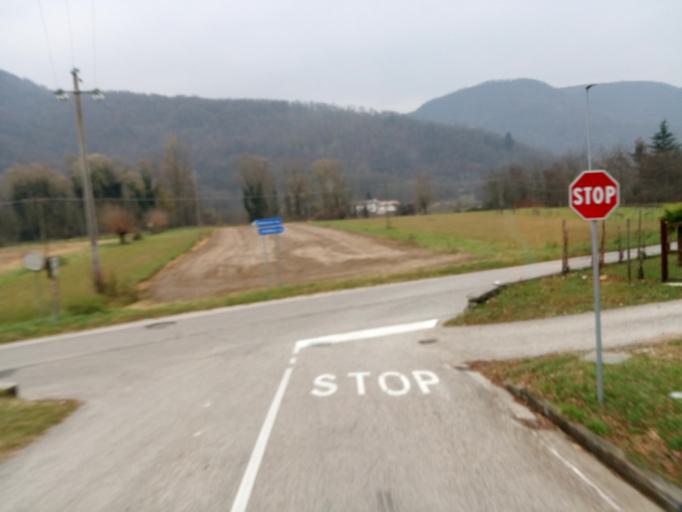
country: IT
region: Friuli Venezia Giulia
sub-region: Provincia di Udine
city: Merso di Sopra
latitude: 46.1180
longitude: 13.5111
